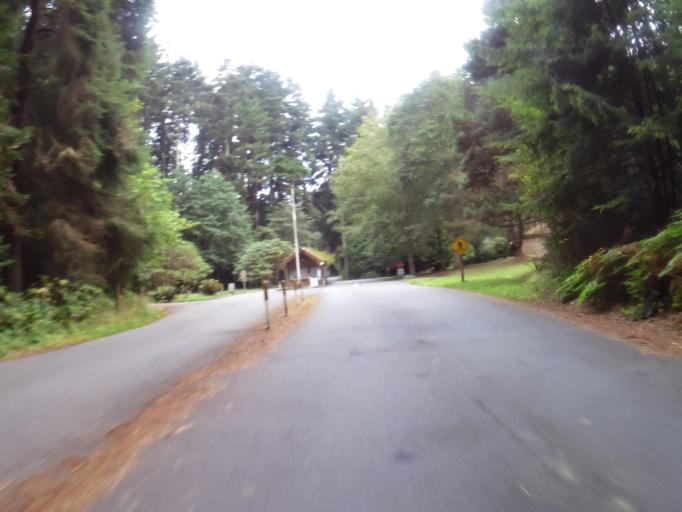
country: US
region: California
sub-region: Humboldt County
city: Westhaven-Moonstone
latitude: 41.1344
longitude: -124.1545
